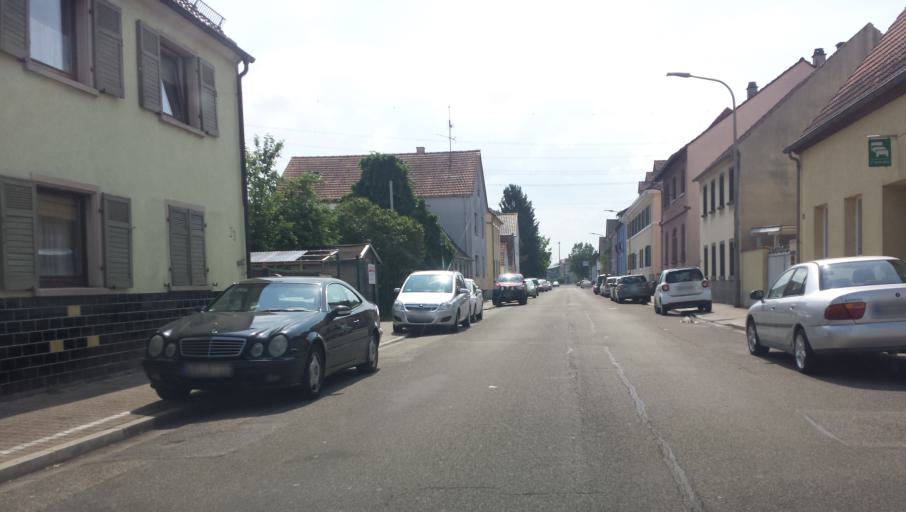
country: DE
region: Rheinland-Pfalz
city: Worth am Rhein
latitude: 49.0489
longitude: 8.2696
